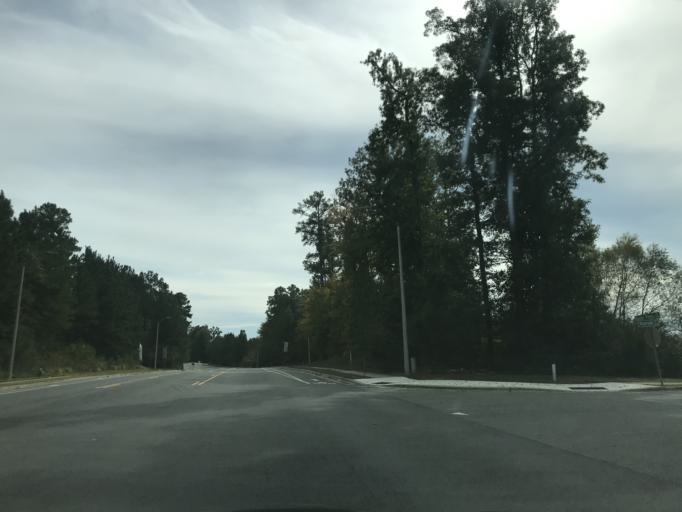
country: US
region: North Carolina
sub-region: Wake County
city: Wake Forest
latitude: 35.9514
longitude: -78.5457
